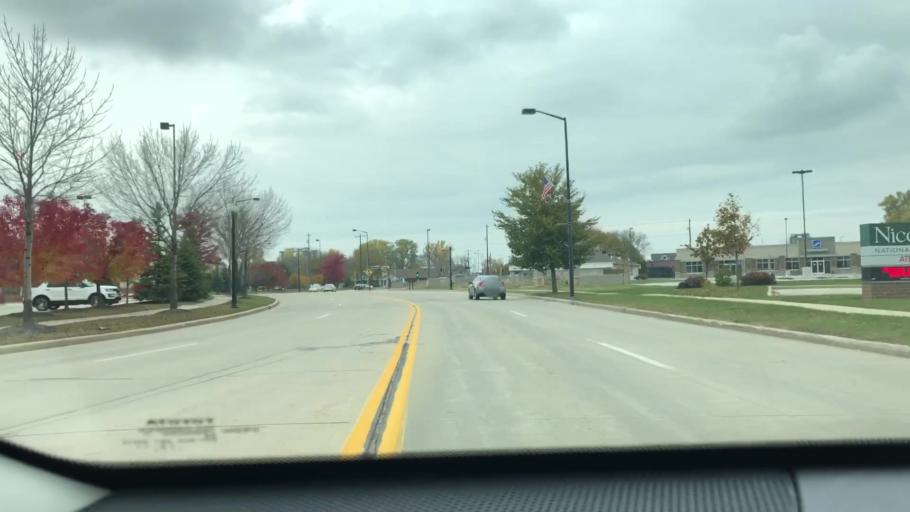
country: US
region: Wisconsin
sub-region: Brown County
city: Ashwaubenon
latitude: 44.4856
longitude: -88.0605
